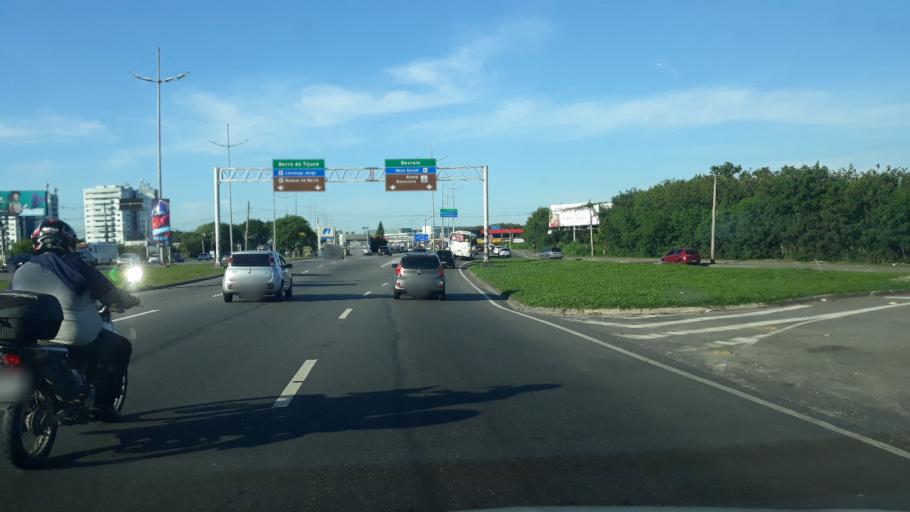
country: BR
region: Rio de Janeiro
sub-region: Rio De Janeiro
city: Rio de Janeiro
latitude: -22.9682
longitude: -43.3584
